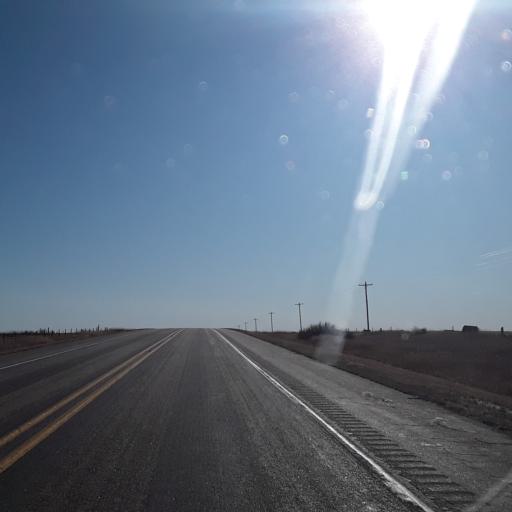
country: US
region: Nebraska
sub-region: Frontier County
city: Stockville
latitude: 40.5777
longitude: -100.6297
